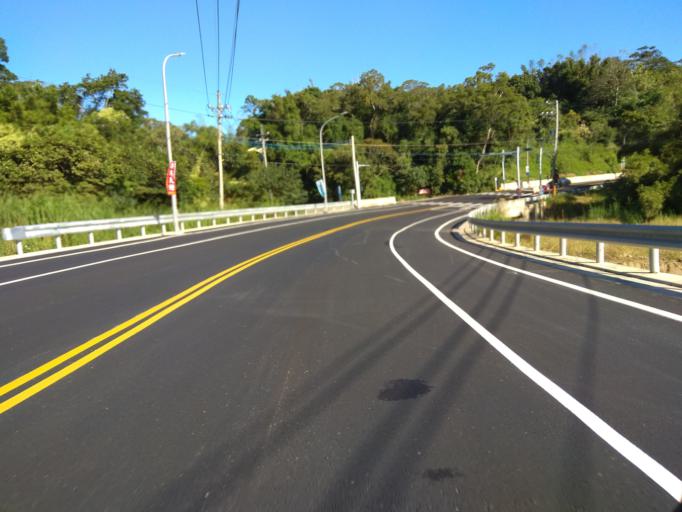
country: TW
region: Taiwan
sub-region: Hsinchu
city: Zhubei
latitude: 24.8497
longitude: 121.1177
